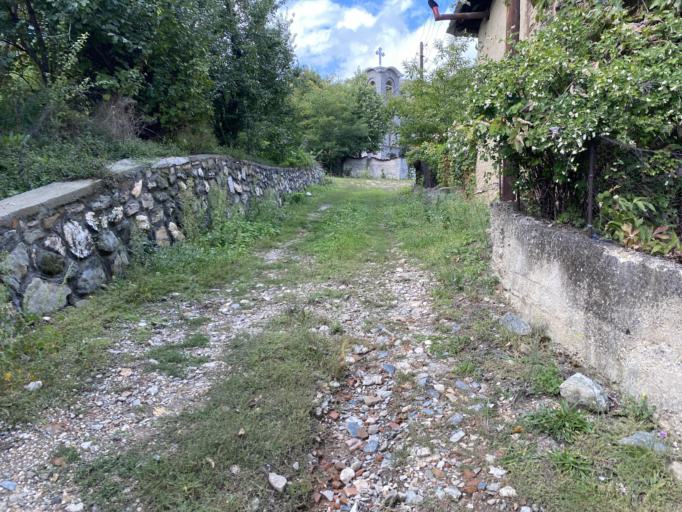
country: MK
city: Radishani
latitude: 42.1092
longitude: 21.4541
